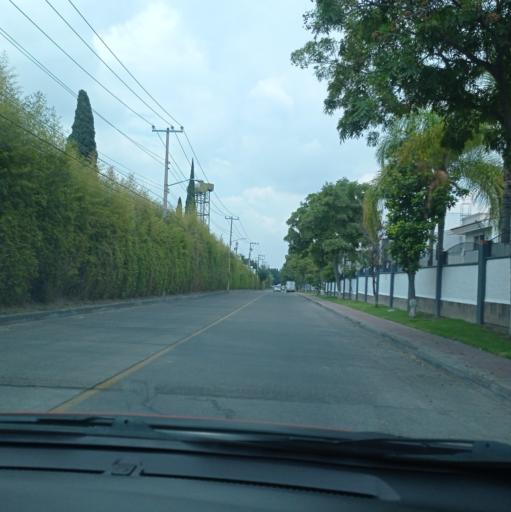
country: MX
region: Jalisco
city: Zapopan2
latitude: 20.6882
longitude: -103.4536
